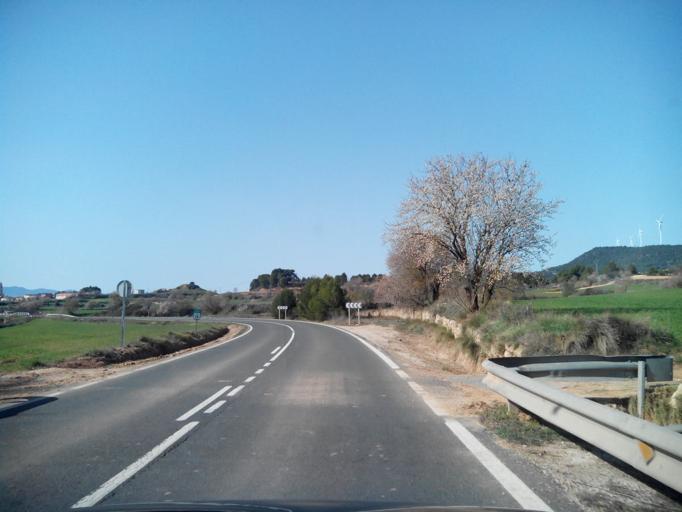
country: ES
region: Catalonia
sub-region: Provincia de Tarragona
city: Conesa
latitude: 41.4842
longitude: 1.2924
